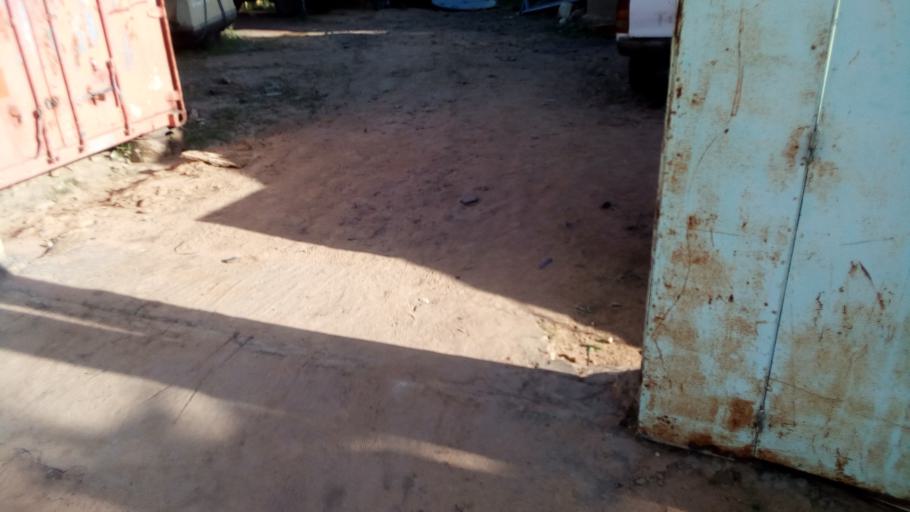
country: ML
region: Kayes
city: Kayes
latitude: 14.4397
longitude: -11.4594
